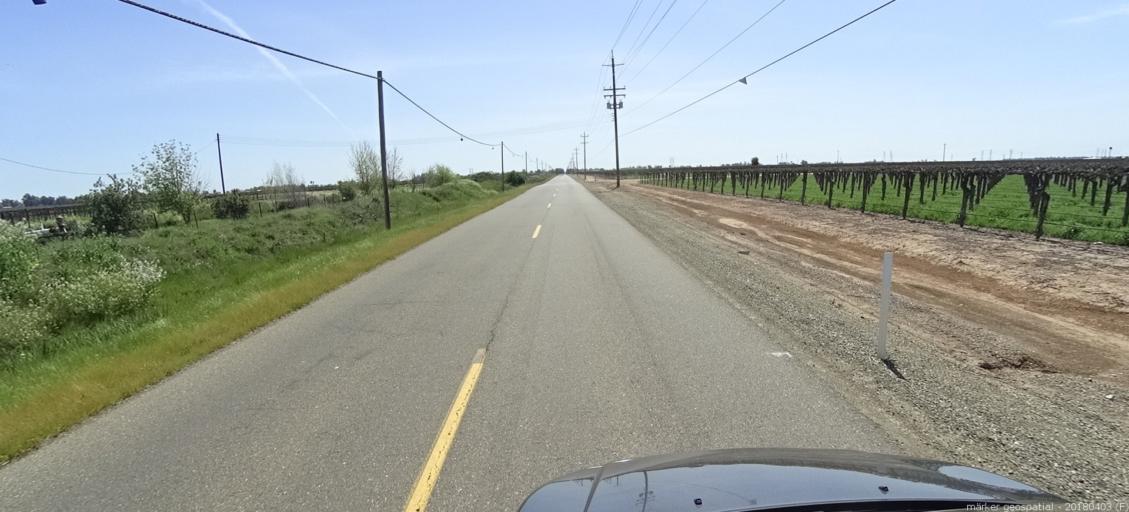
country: US
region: California
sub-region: Sacramento County
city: Wilton
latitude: 38.3687
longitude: -121.2421
